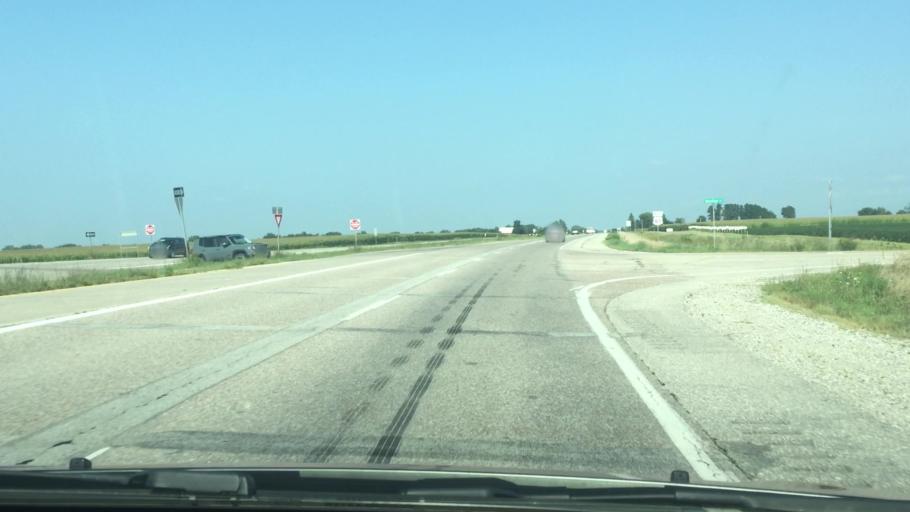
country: US
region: Iowa
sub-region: Muscatine County
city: Wilton
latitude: 41.4981
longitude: -90.9691
